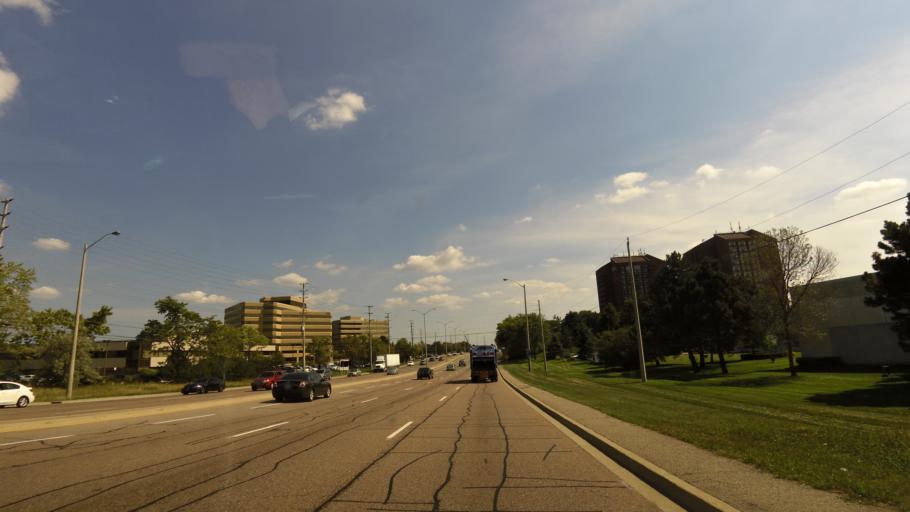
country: CA
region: Ontario
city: Brampton
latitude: 43.6037
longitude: -79.7439
